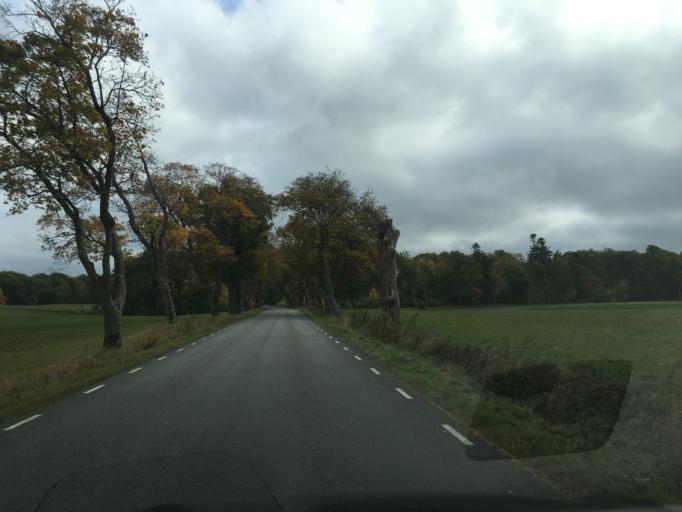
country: SE
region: Skane
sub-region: Tomelilla Kommun
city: Tomelilla
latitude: 55.6457
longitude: 14.0411
